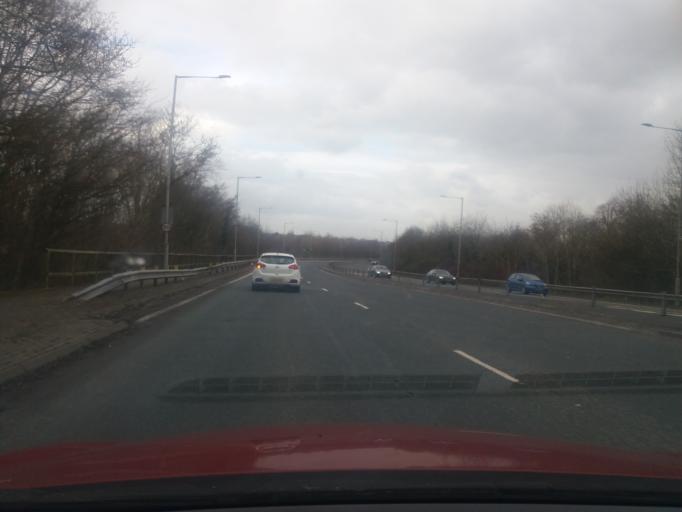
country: GB
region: England
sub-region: Lancashire
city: Preston
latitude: 53.7434
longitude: -2.6837
